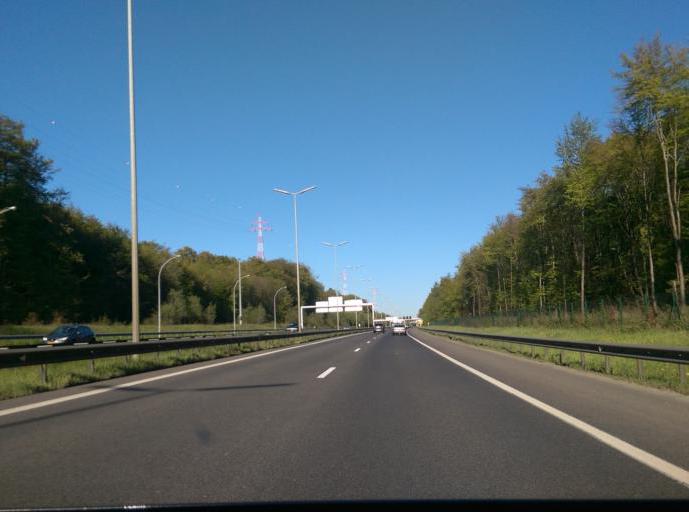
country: LU
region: Luxembourg
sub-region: Canton de Luxembourg
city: Sandweiler
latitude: 49.6415
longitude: 6.1961
